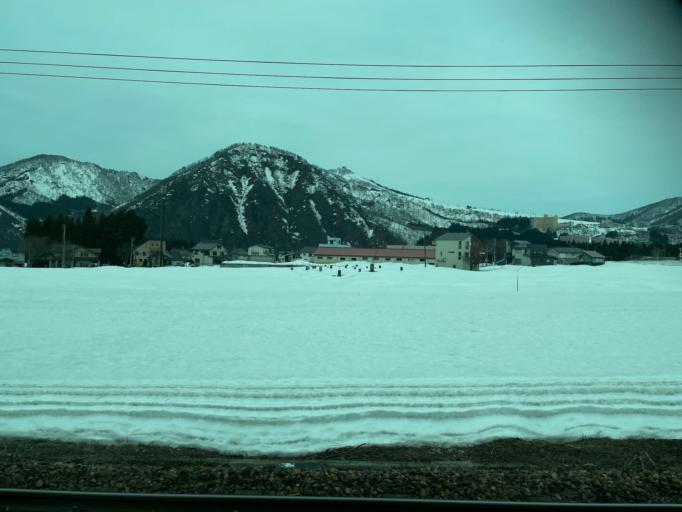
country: JP
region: Niigata
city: Shiozawa
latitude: 36.9254
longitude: 138.8267
